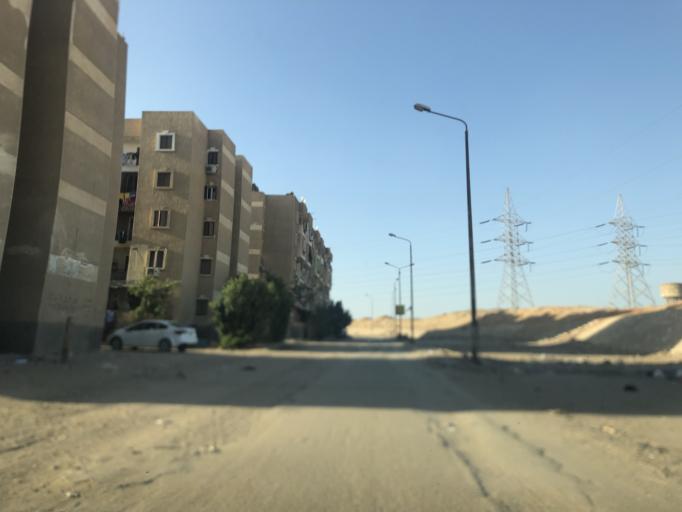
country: EG
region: Al Jizah
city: Al Jizah
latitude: 29.9862
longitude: 31.1094
